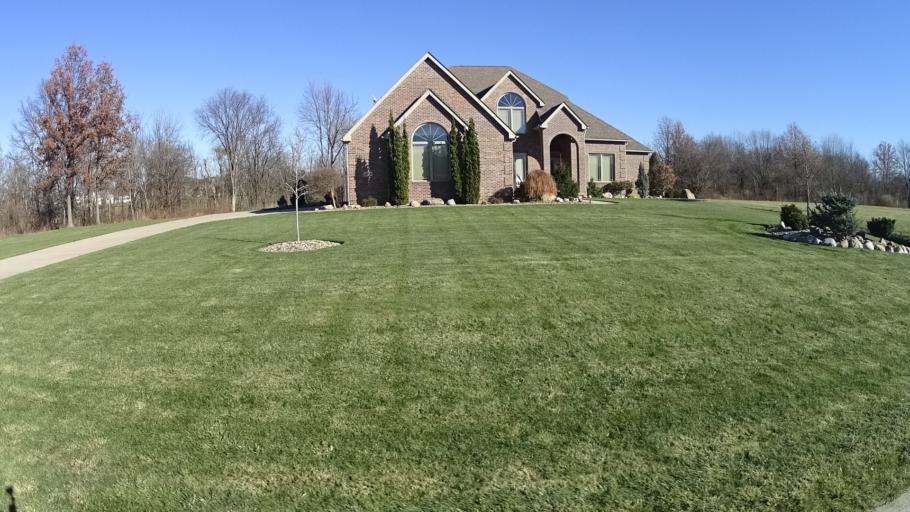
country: US
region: Ohio
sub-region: Lorain County
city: Lagrange
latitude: 41.2960
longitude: -82.1207
